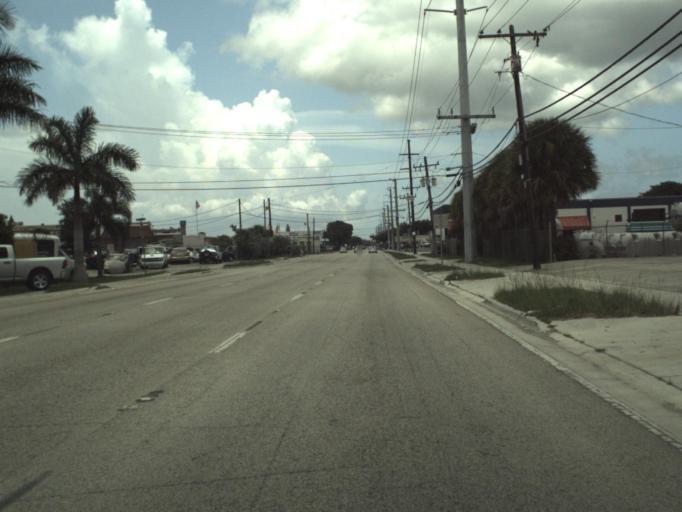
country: US
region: Florida
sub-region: Broward County
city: Pompano Beach
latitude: 26.2145
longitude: -80.1313
